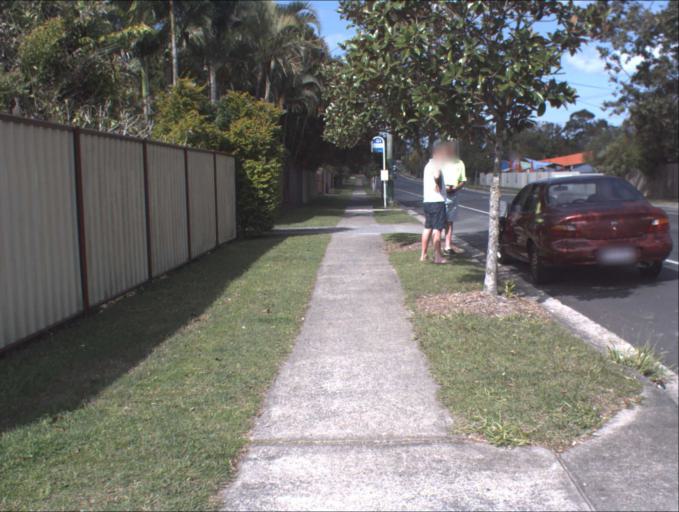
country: AU
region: Queensland
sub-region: Logan
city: Waterford West
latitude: -27.6856
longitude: 153.1174
